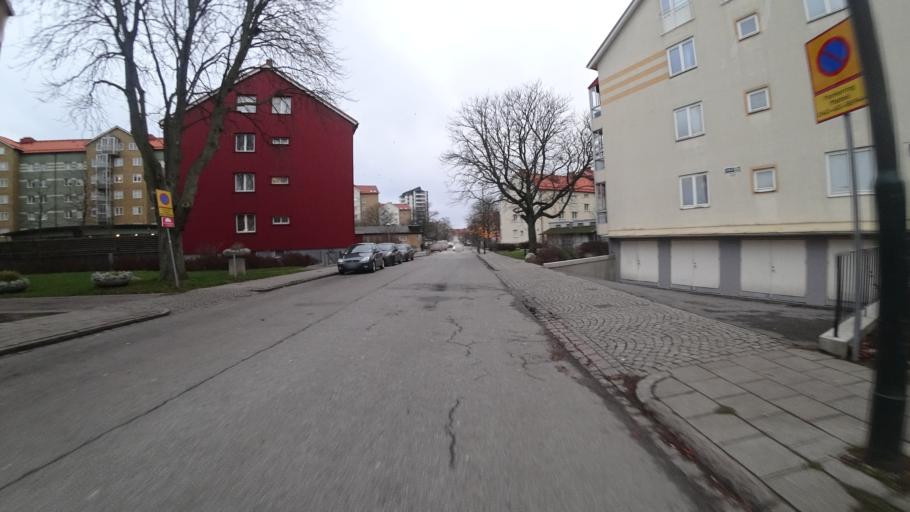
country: SE
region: Skane
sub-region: Malmo
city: Malmoe
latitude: 55.5802
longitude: 13.0268
